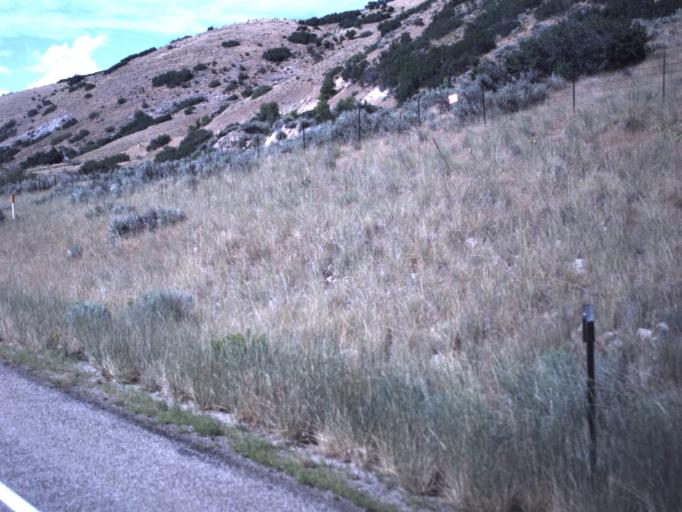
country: US
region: Utah
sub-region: Wasatch County
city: Heber
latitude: 40.4373
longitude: -111.3577
